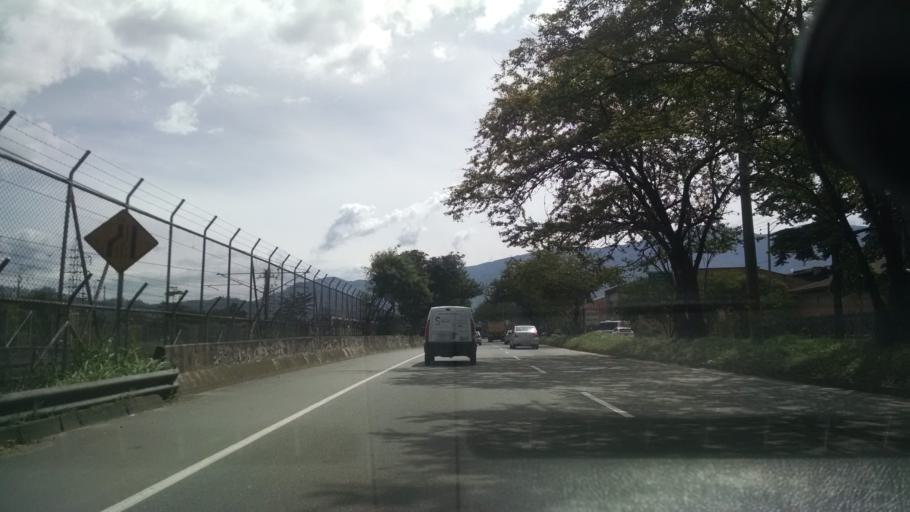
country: CO
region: Antioquia
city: Envigado
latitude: 6.1740
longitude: -75.5982
